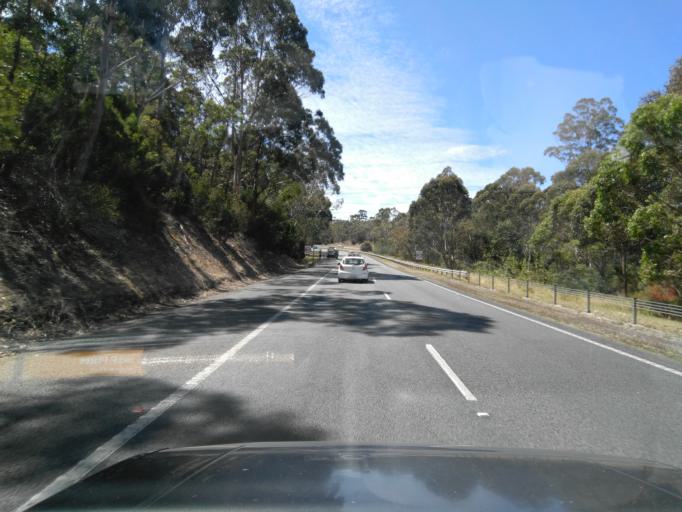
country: AU
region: Tasmania
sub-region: Hobart
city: Dynnyrne
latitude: -42.9174
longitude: 147.3090
